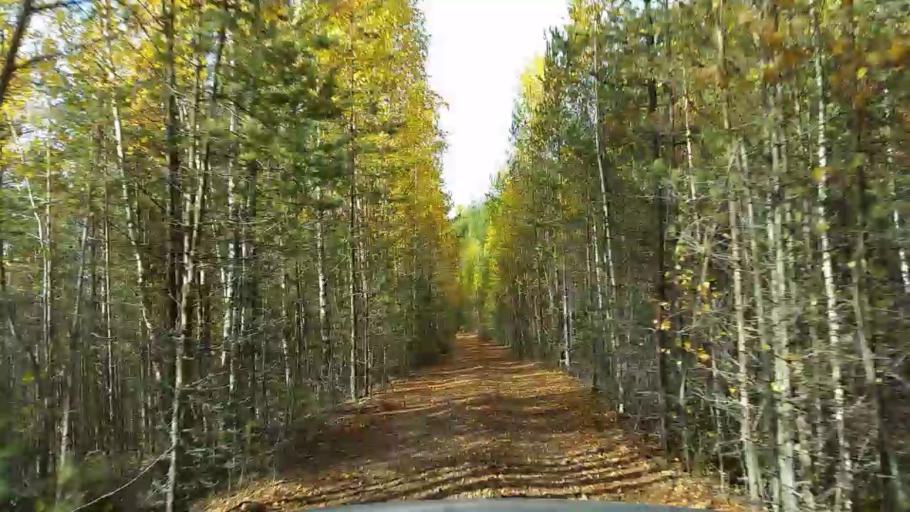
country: SE
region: Gaevleborg
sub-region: Ljusdals Kommun
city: Jaervsoe
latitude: 61.7812
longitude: 16.1936
